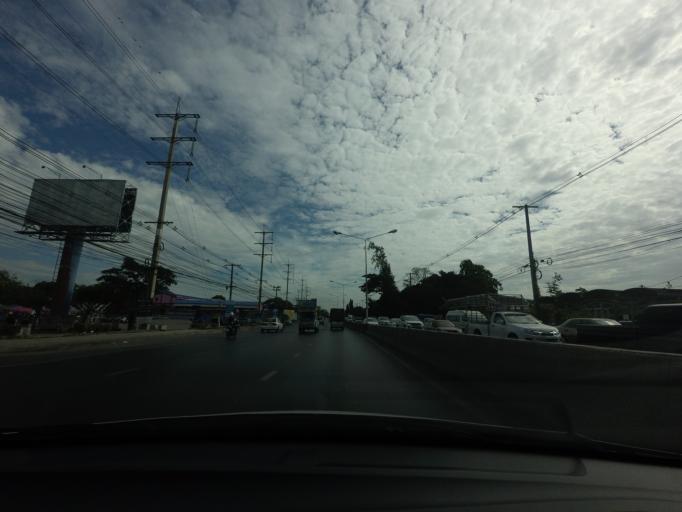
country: TH
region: Pathum Thani
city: Thanyaburi
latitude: 14.0208
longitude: 100.7361
